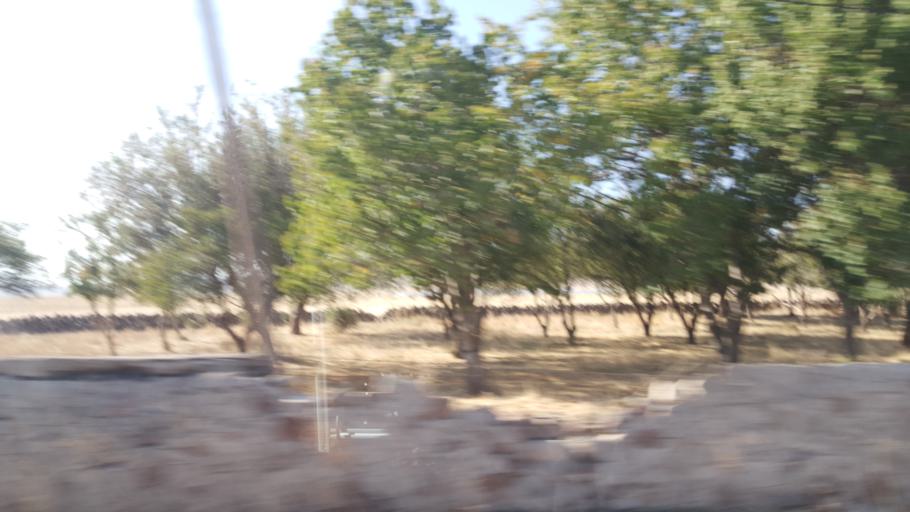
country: TR
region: Ankara
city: Altpinar
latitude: 39.2655
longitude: 32.7535
